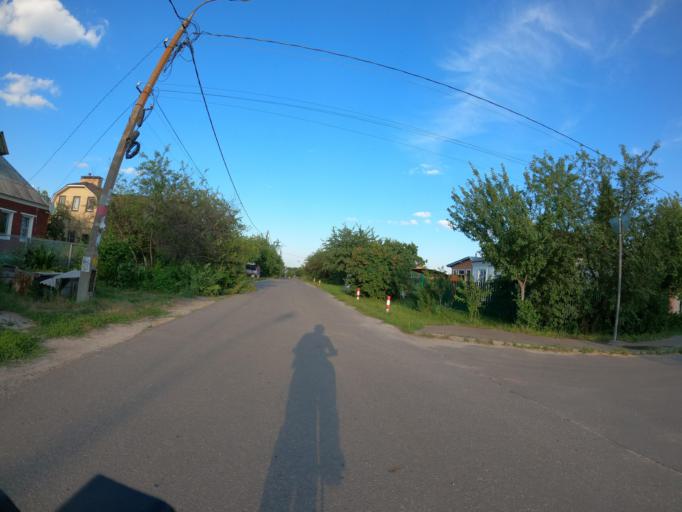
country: RU
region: Moskovskaya
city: Raduzhnyy
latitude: 55.1040
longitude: 38.7241
